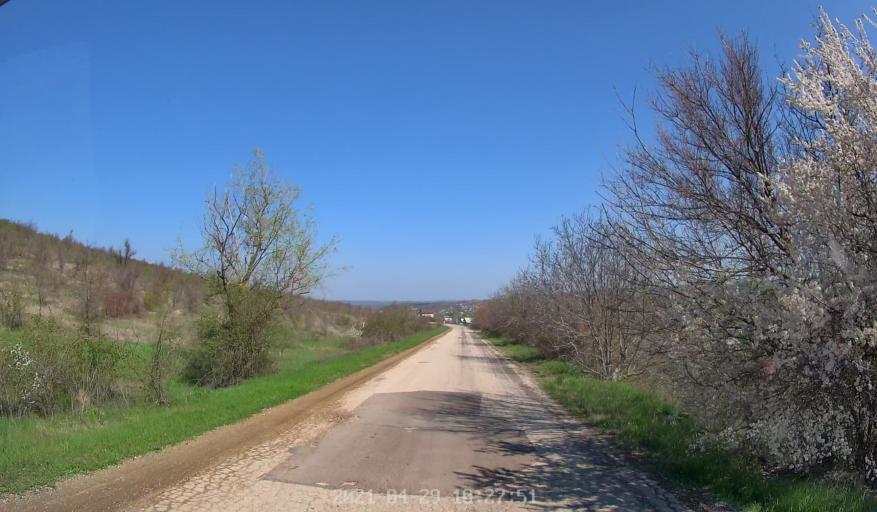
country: MD
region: Chisinau
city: Ciorescu
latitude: 47.1516
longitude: 28.9598
